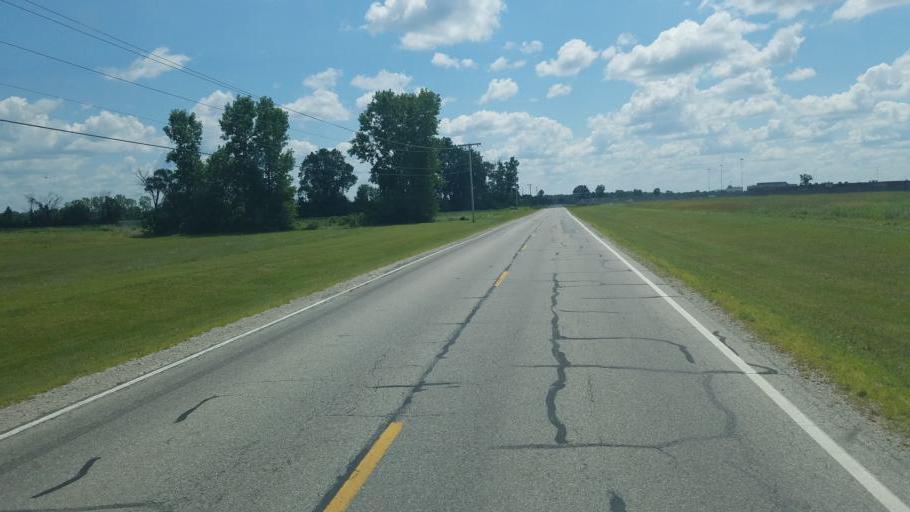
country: US
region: Ohio
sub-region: Marion County
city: Marion
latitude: 40.6250
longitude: -83.1014
